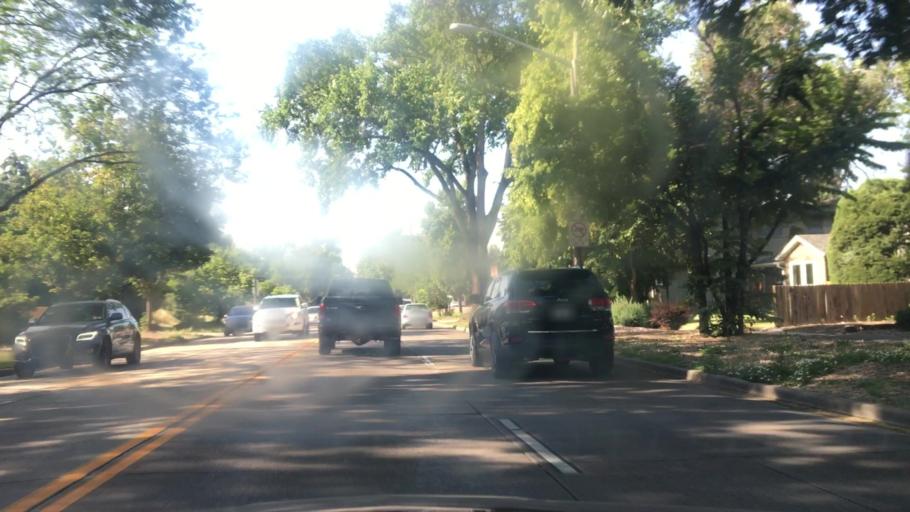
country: US
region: Colorado
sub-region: Arapahoe County
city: Glendale
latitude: 39.6907
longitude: -104.9594
